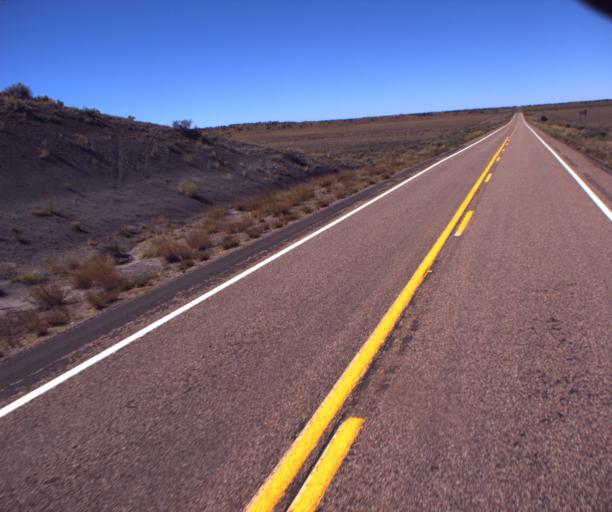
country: US
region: Arizona
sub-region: Apache County
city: Saint Johns
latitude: 34.5879
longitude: -109.5891
